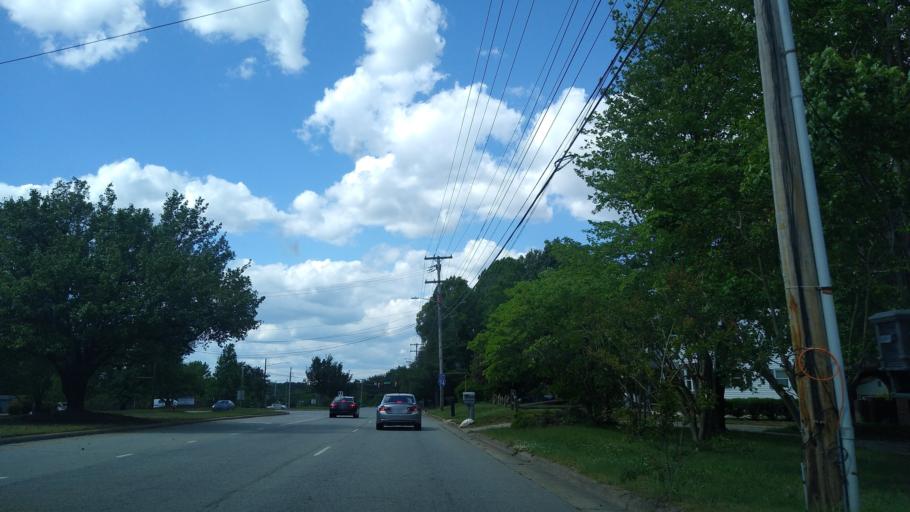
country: US
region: North Carolina
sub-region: Guilford County
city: High Point
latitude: 36.0068
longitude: -80.0099
